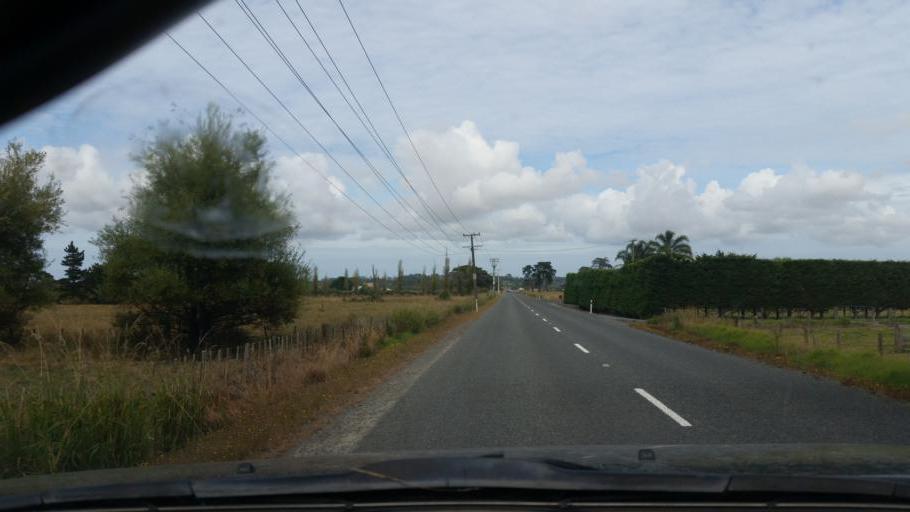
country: NZ
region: Northland
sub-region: Kaipara District
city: Dargaville
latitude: -35.9508
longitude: 173.8988
